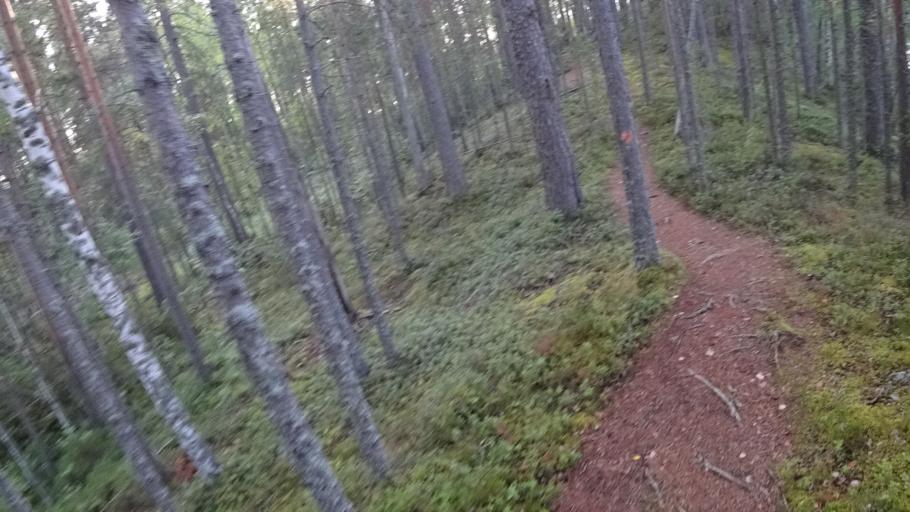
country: FI
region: North Karelia
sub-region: Joensuu
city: Ilomantsi
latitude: 62.5798
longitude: 31.1583
